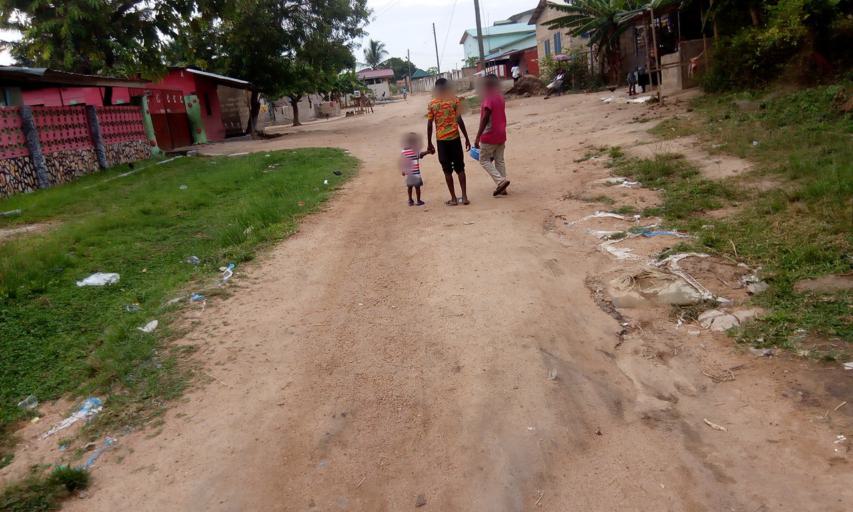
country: GH
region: Central
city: Winneba
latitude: 5.3559
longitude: -0.6219
